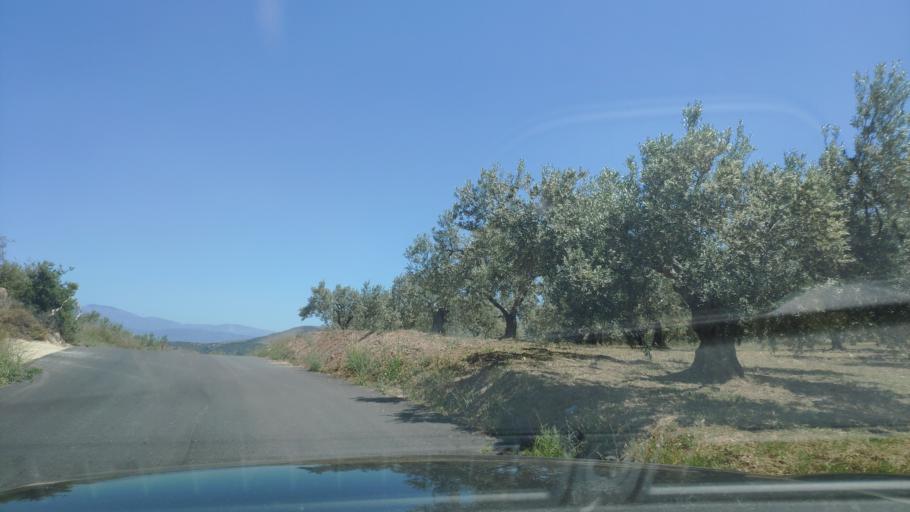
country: GR
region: Peloponnese
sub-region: Nomos Korinthias
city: Khiliomodhi
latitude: 37.8023
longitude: 22.8998
